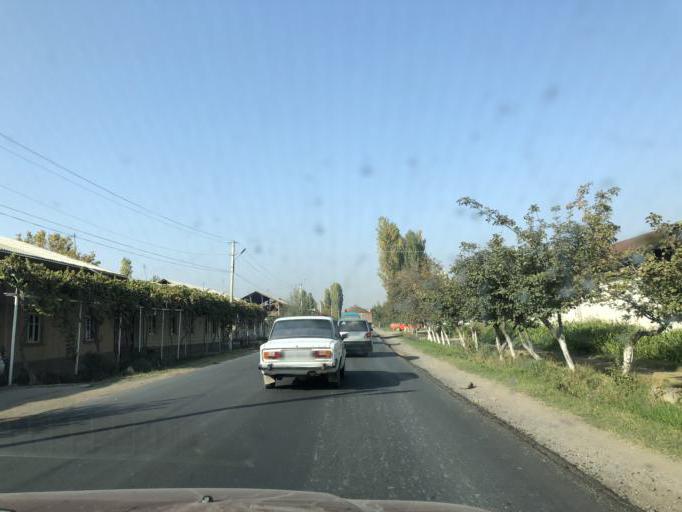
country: UZ
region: Namangan
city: Chust Shahri
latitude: 41.0684
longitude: 71.2047
